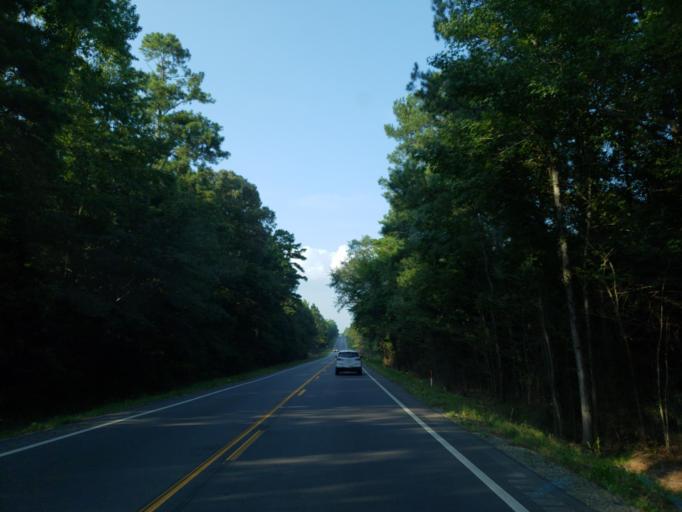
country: US
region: Alabama
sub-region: Greene County
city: Eutaw
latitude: 32.8665
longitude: -87.8727
